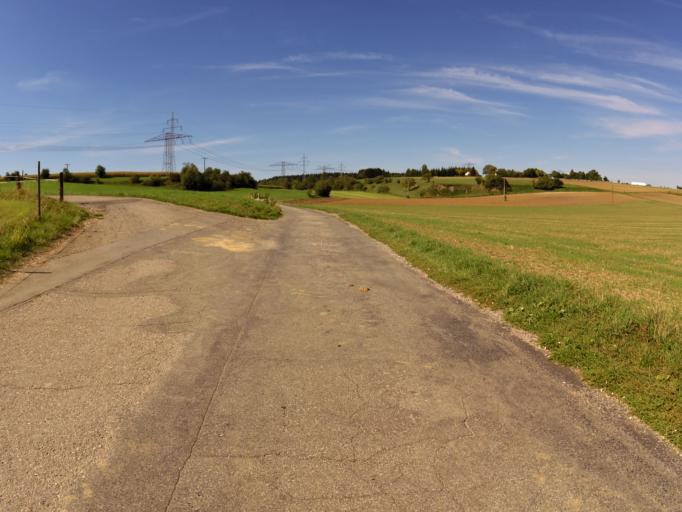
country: DE
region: Baden-Wuerttemberg
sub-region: Freiburg Region
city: Donaueschingen
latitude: 47.9701
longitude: 8.5050
